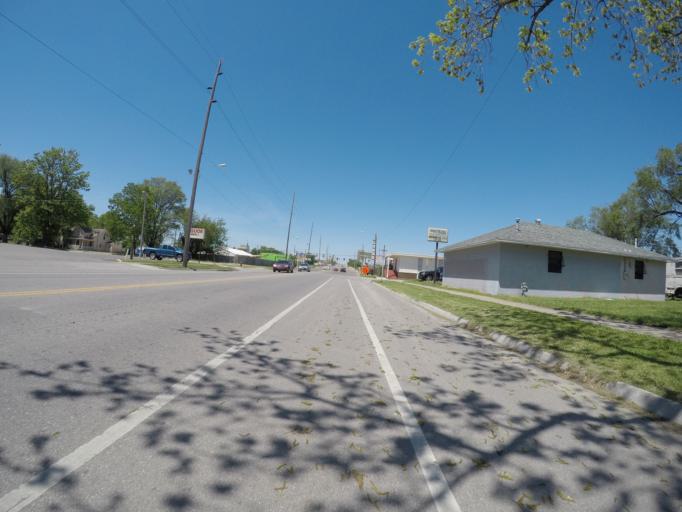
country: US
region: Kansas
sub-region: Shawnee County
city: Topeka
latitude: 39.0482
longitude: -95.6595
